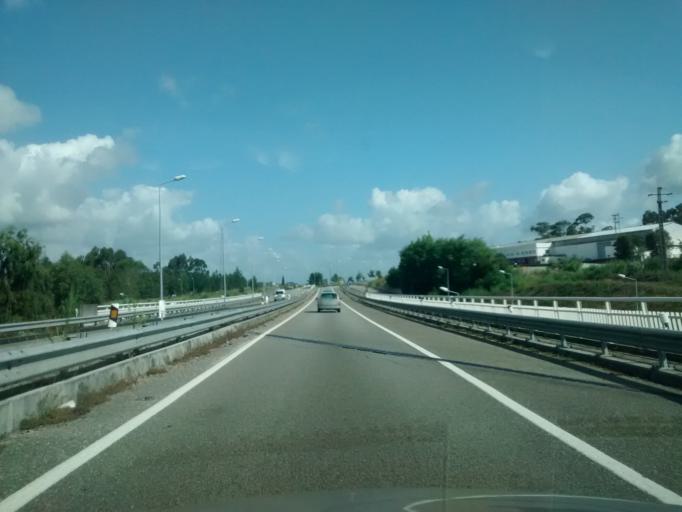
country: PT
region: Aveiro
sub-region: Oliveira do Bairro
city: Oliveira do Bairro
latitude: 40.5217
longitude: -8.5051
